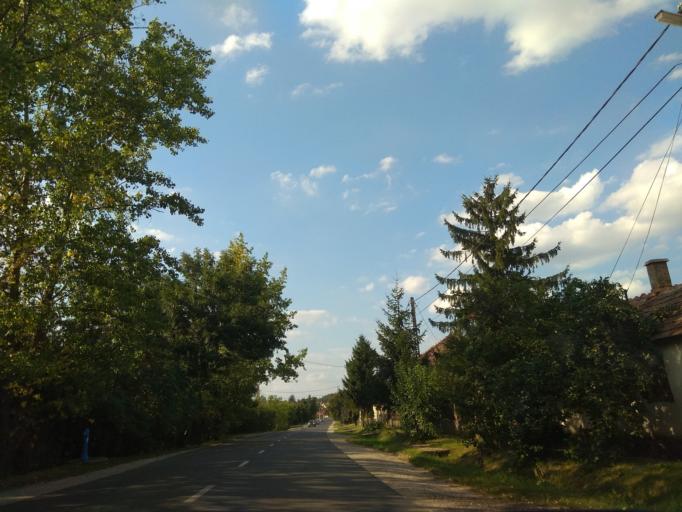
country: HU
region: Borsod-Abauj-Zemplen
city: Harsany
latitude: 47.9585
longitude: 20.7438
